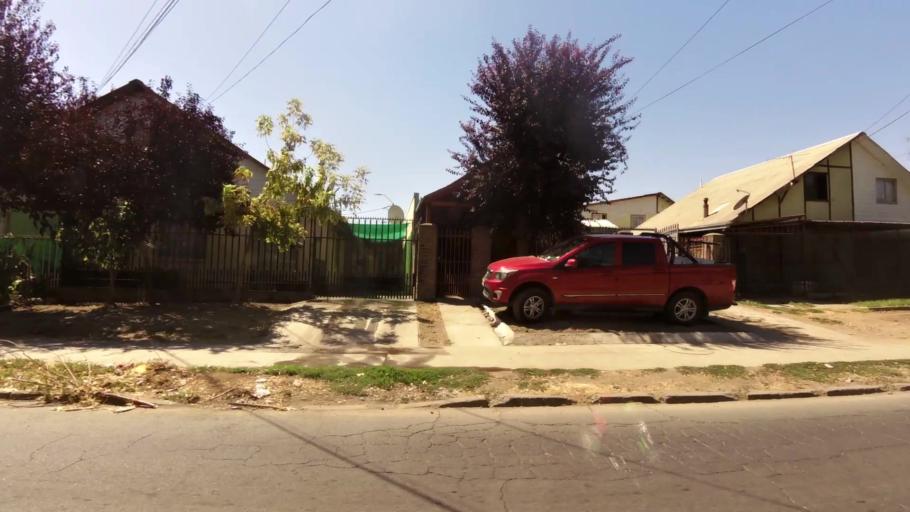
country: CL
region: Maule
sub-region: Provincia de Curico
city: Curico
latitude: -34.9678
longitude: -71.2413
